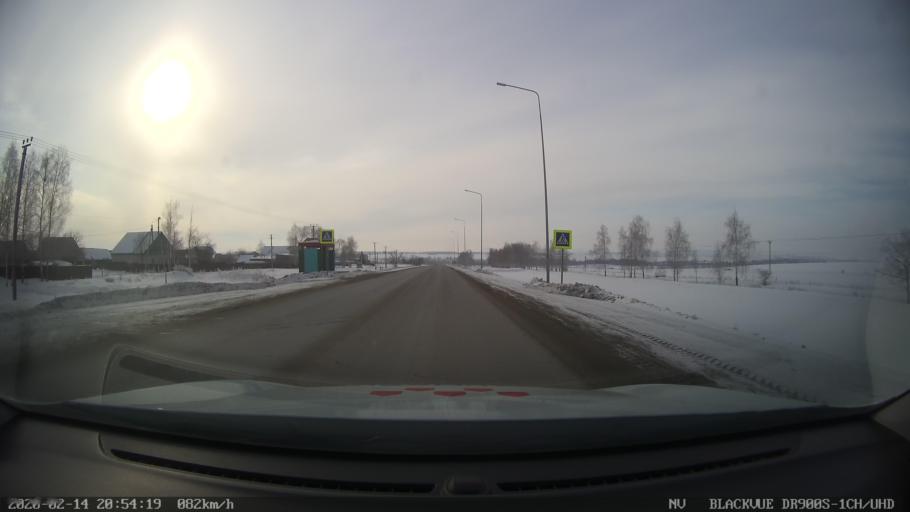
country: RU
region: Tatarstan
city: Kuybyshevskiy Zaton
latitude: 55.1871
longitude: 49.2432
